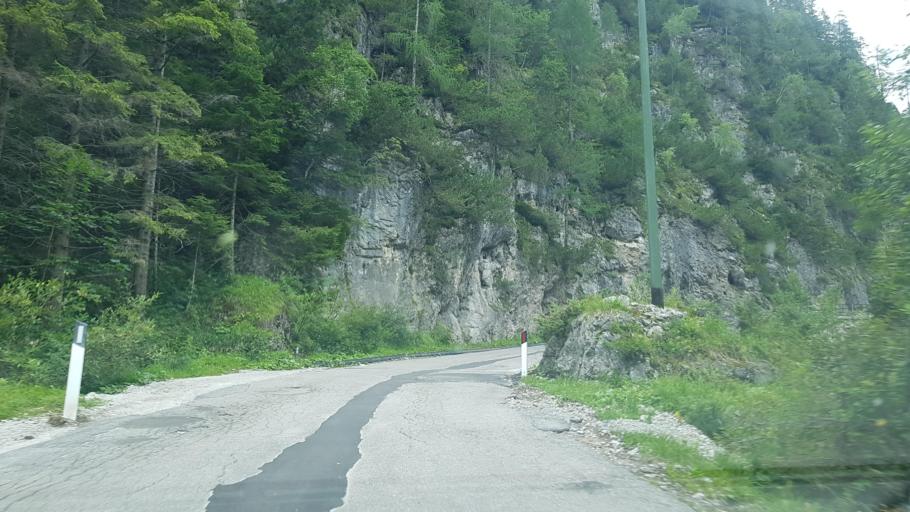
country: IT
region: Veneto
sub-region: Provincia di Belluno
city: San Pietro di Cadore
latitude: 46.5960
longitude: 12.6299
